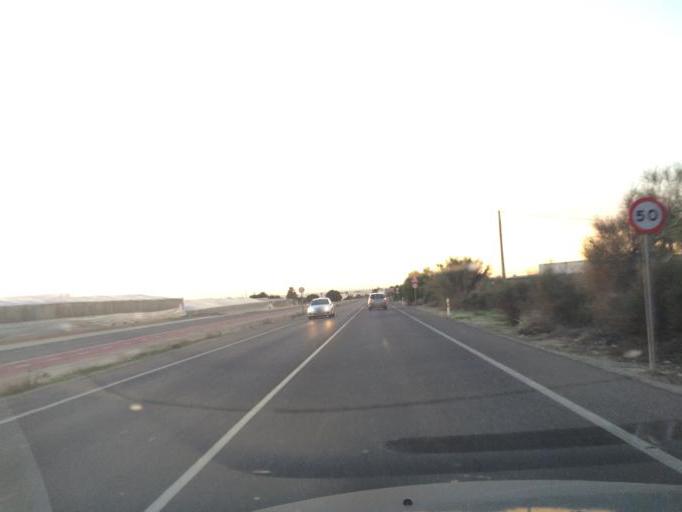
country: ES
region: Andalusia
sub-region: Provincia de Almeria
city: Almeria
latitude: 36.8365
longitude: -2.4171
